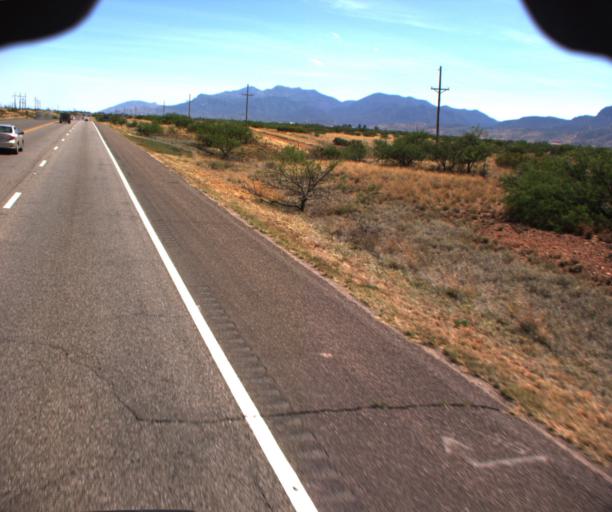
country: US
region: Arizona
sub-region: Cochise County
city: Sierra Vista
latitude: 31.5847
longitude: -110.3202
